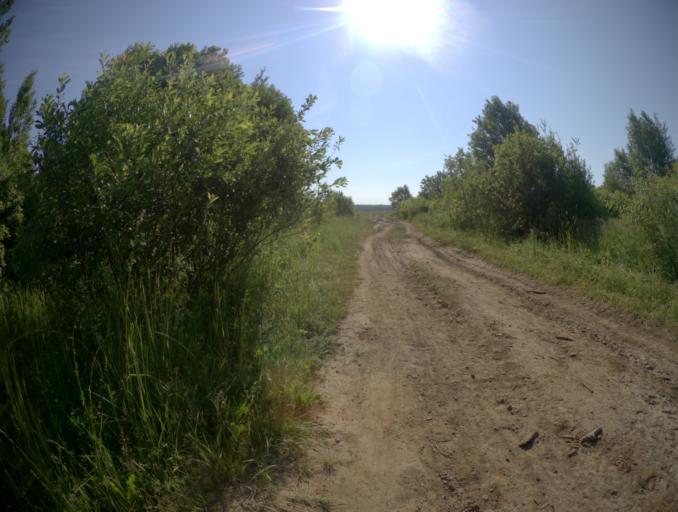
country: RU
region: Vladimir
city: Novovyazniki
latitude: 56.1937
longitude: 42.1904
